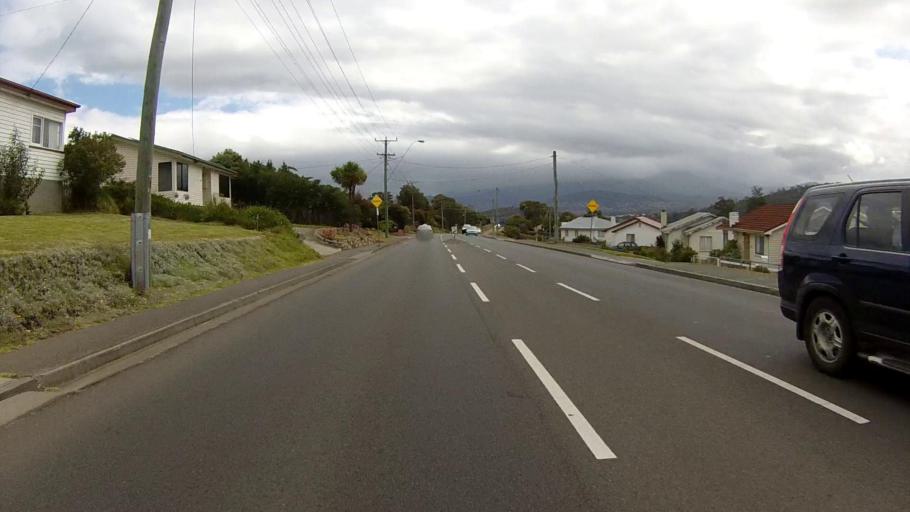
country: AU
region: Tasmania
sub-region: Clarence
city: Warrane
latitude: -42.8590
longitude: 147.3843
